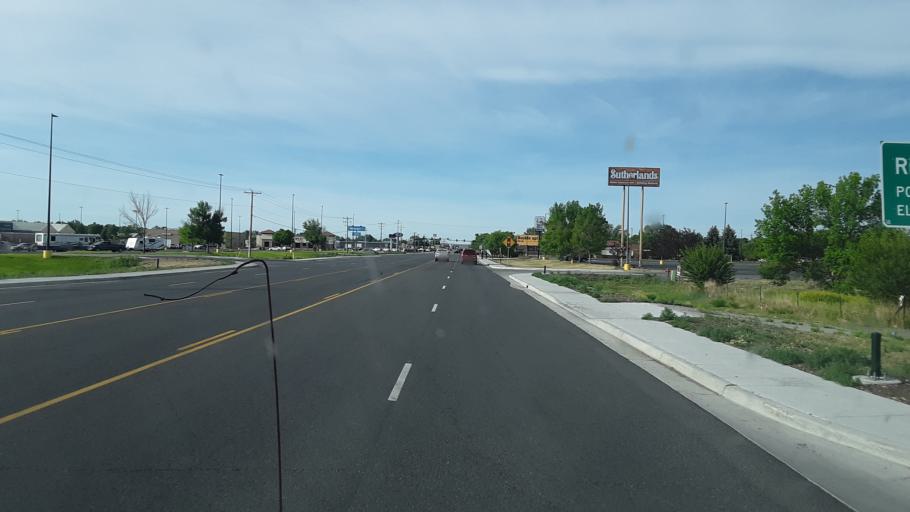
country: US
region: Wyoming
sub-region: Fremont County
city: Riverton
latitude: 43.0446
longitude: -108.3807
